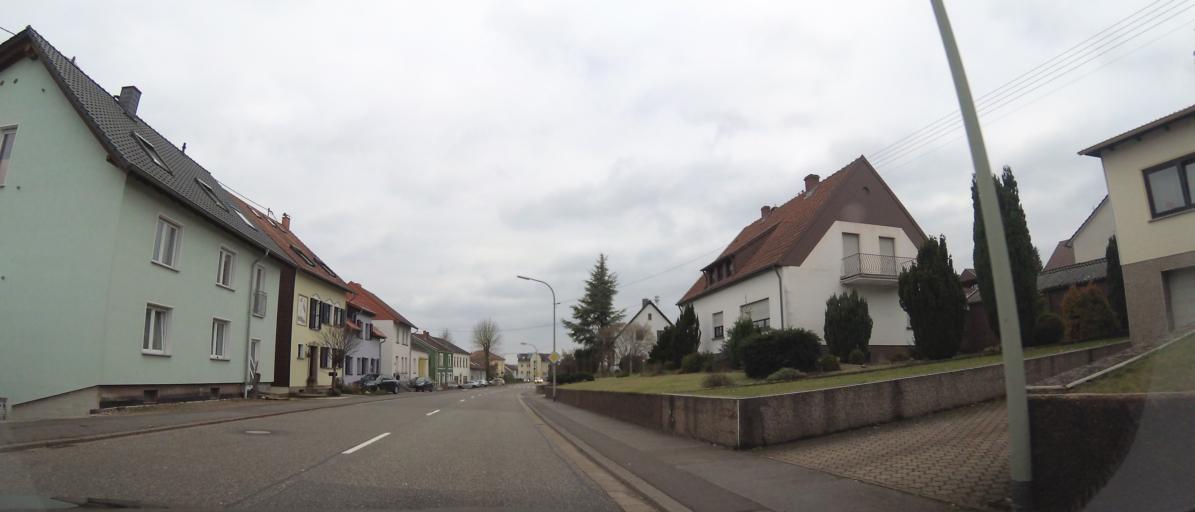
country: DE
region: Saarland
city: Schwalbach
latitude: 49.3003
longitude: 6.8472
